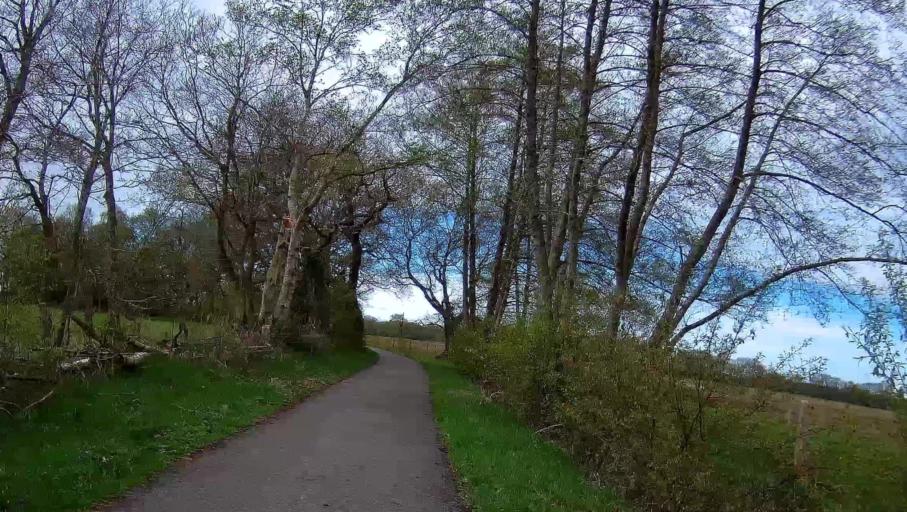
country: NL
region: Drenthe
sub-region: Gemeente Aa en Hunze
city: Anloo
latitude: 52.9637
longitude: 6.7085
